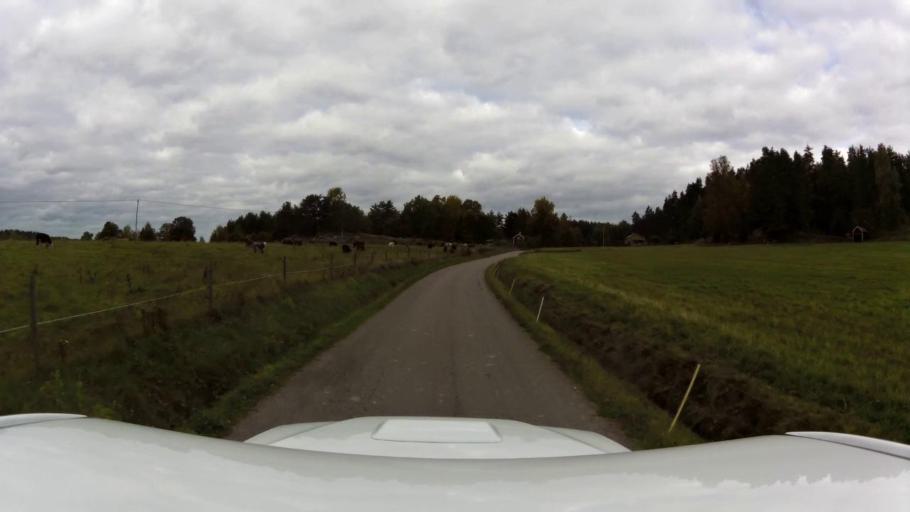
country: SE
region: OEstergoetland
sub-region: Kinda Kommun
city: Rimforsa
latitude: 58.1995
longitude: 15.5751
